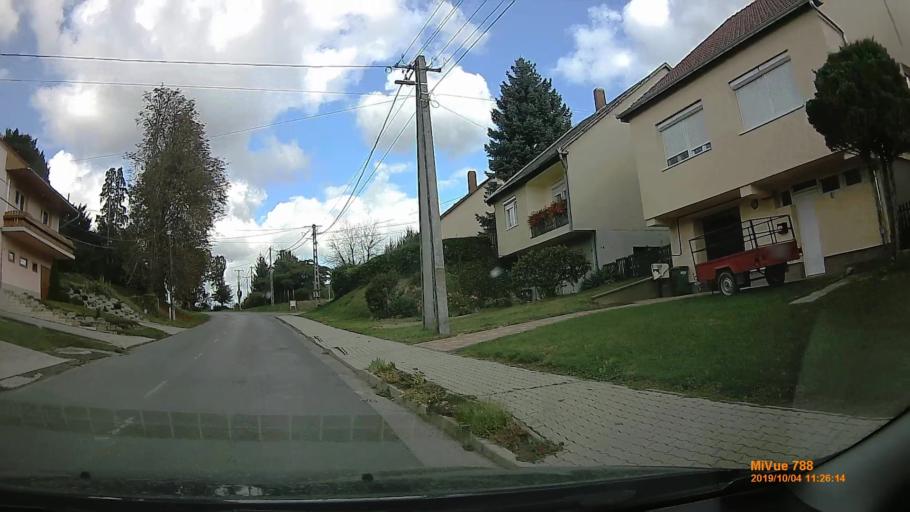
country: HU
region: Somogy
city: Kaposvar
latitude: 46.5081
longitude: 17.8156
